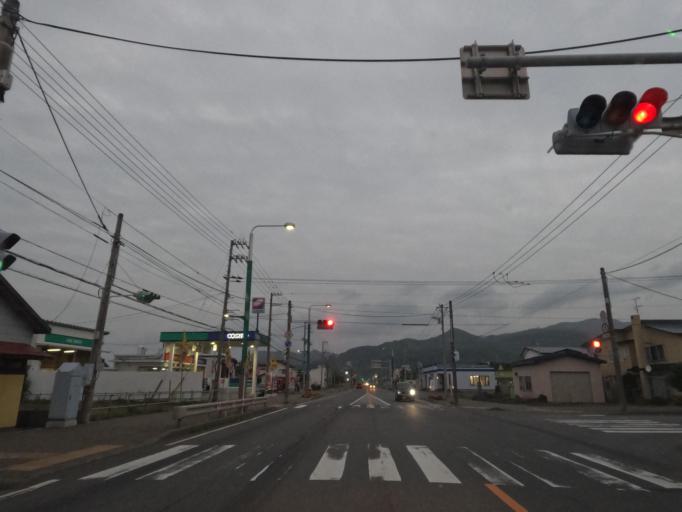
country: JP
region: Hokkaido
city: Date
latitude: 42.5402
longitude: 140.7718
